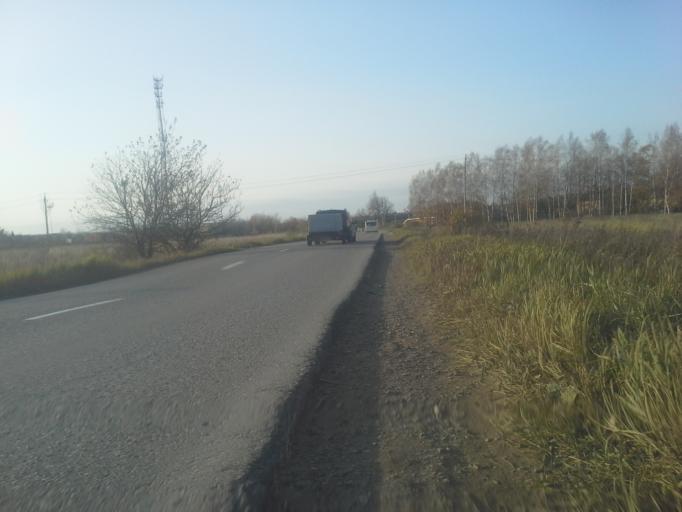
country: RU
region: Moskovskaya
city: Krasnoznamensk
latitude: 55.5945
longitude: 37.0149
